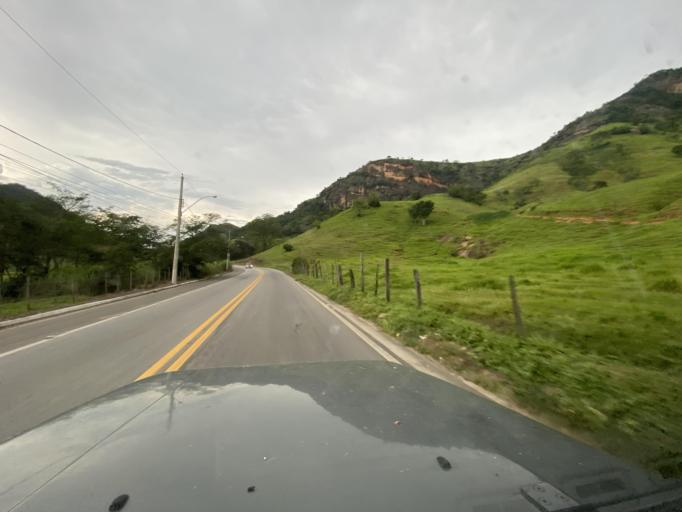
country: BR
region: Espirito Santo
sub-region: Jeronimo Monteiro
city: Jeronimo Monteiro
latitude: -20.8023
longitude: -41.3537
